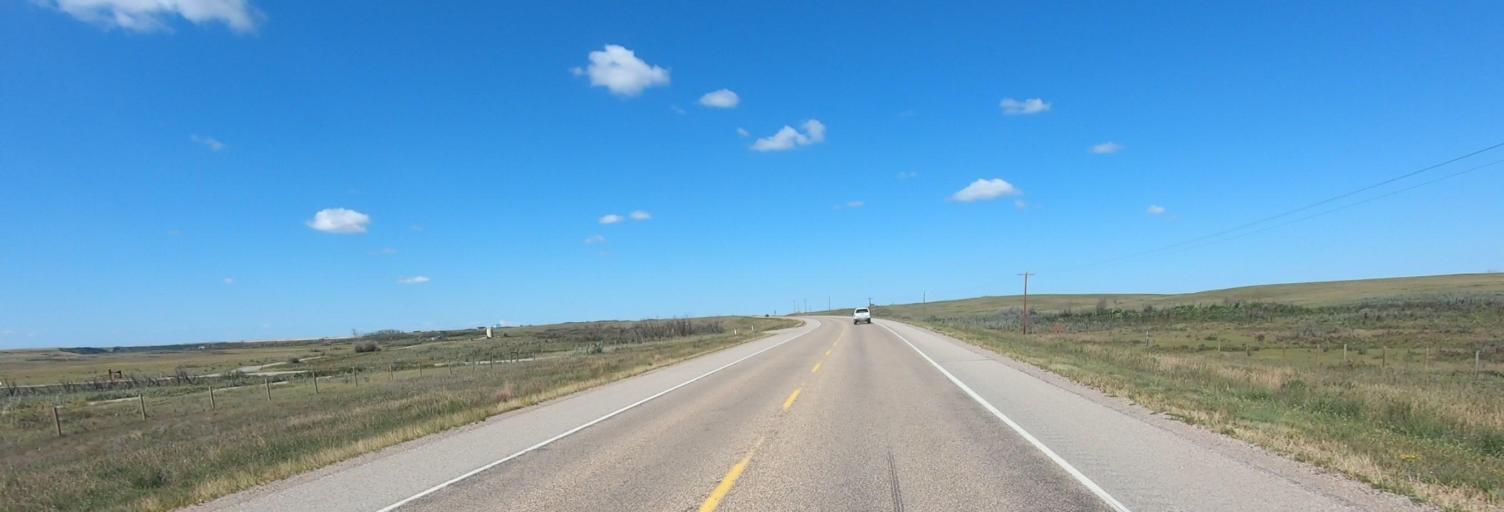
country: CA
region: Alberta
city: Strathmore
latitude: 50.8698
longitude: -113.1542
